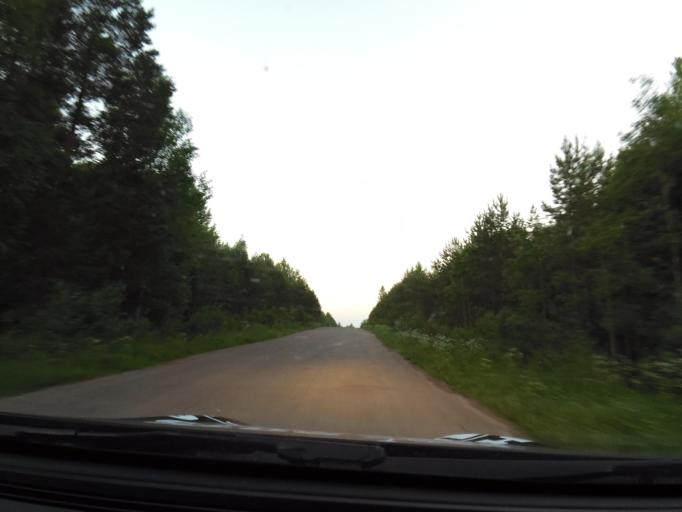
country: RU
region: Vologda
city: Vytegra
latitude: 60.8674
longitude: 35.9685
